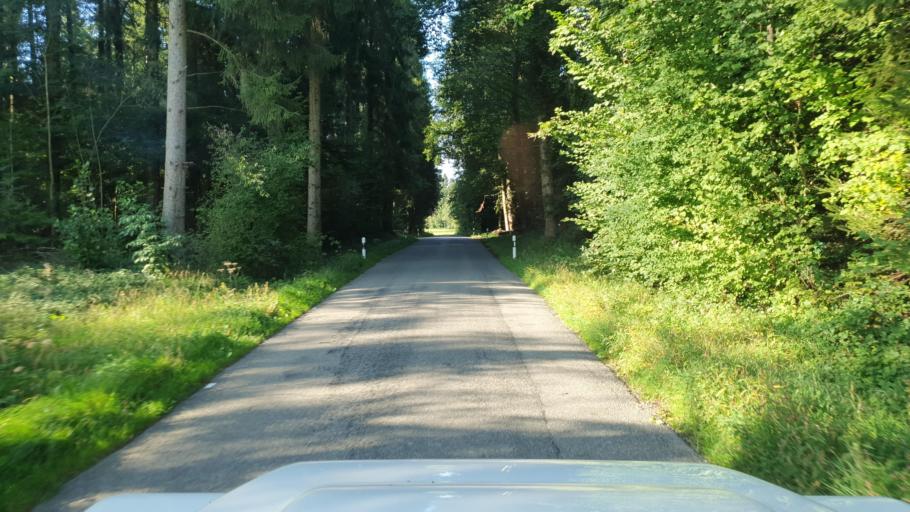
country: CH
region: Aargau
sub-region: Bezirk Muri
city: Oberruti
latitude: 47.1696
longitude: 8.3700
